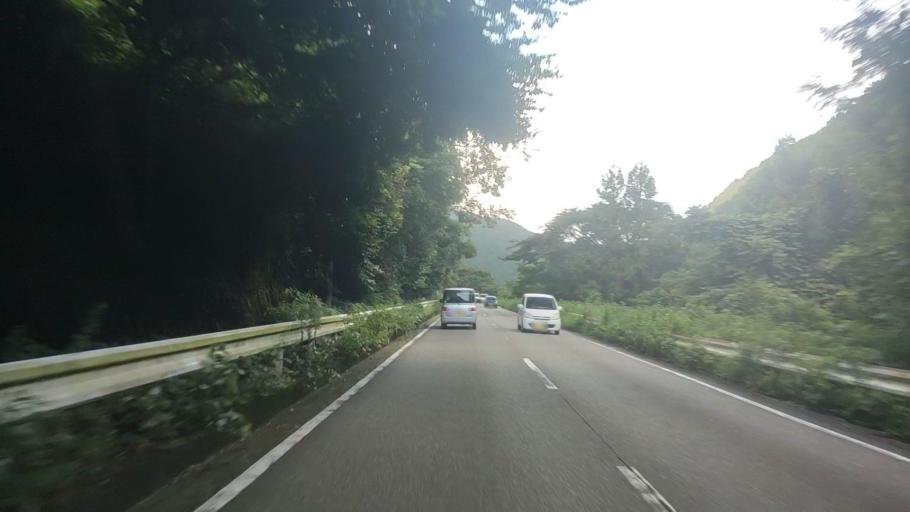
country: JP
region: Wakayama
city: Tanabe
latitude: 33.7642
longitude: 135.5003
